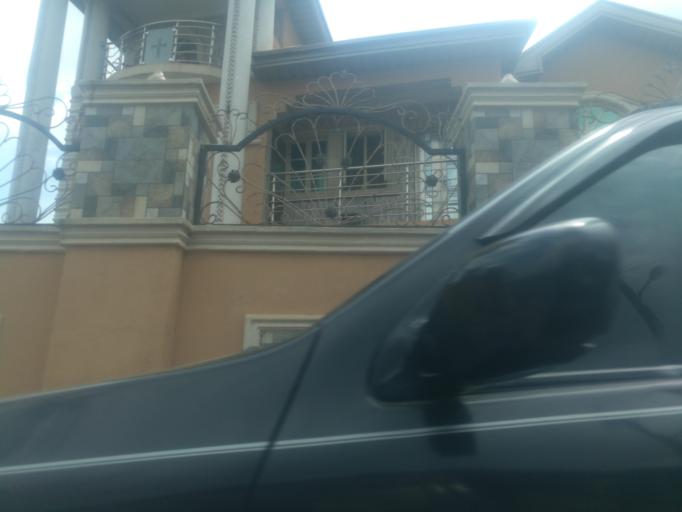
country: NG
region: Oyo
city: Ibadan
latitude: 7.4030
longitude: 3.9272
